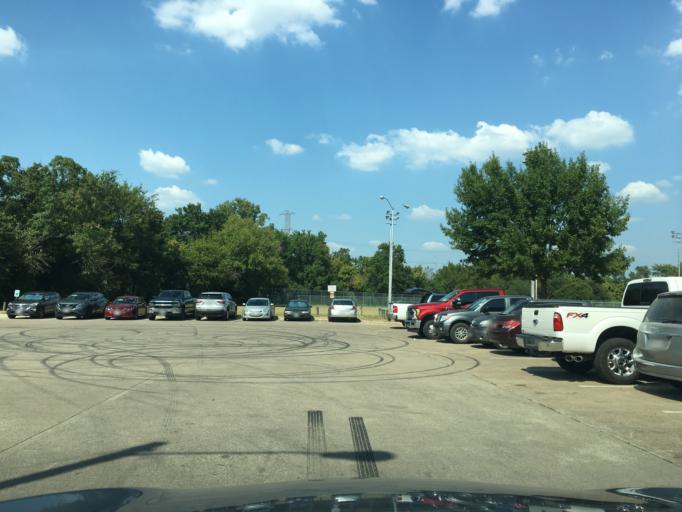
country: US
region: Texas
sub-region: Dallas County
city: Dallas
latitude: 32.7481
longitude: -96.7946
